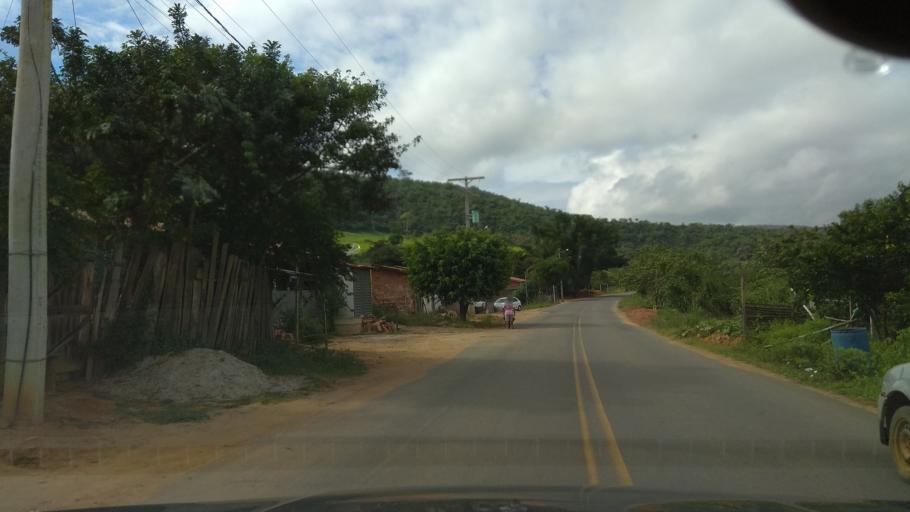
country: BR
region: Bahia
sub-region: Ubaira
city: Ubaira
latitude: -13.2531
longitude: -39.7131
